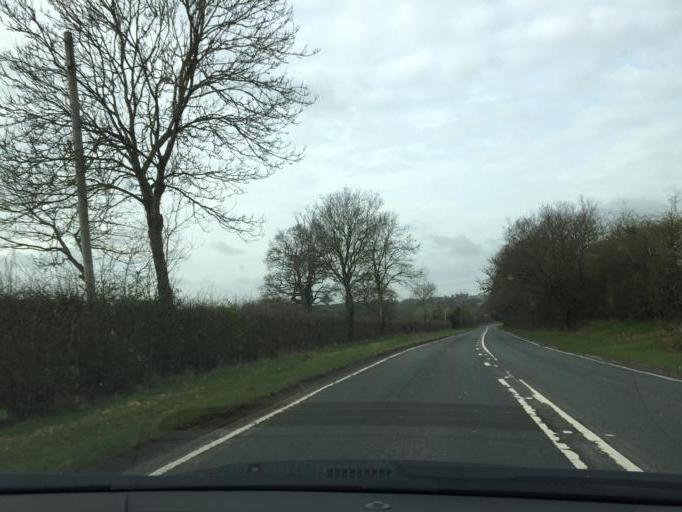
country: GB
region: England
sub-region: Warwickshire
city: Henley in Arden
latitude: 52.2904
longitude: -1.8061
